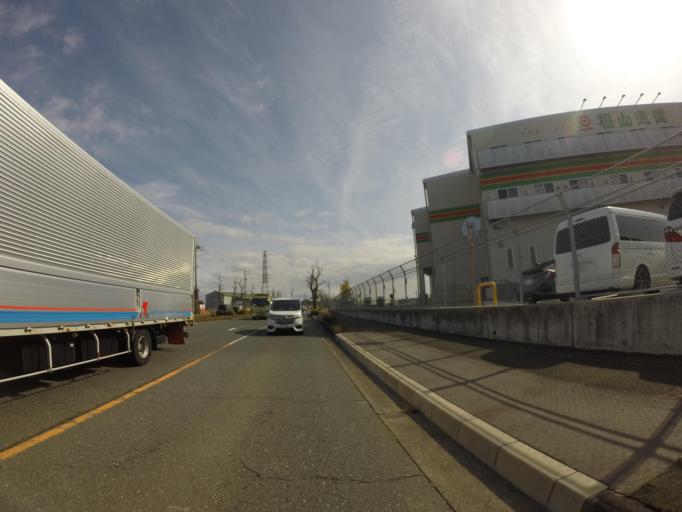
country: JP
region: Shizuoka
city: Hamamatsu
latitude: 34.7739
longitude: 137.6941
